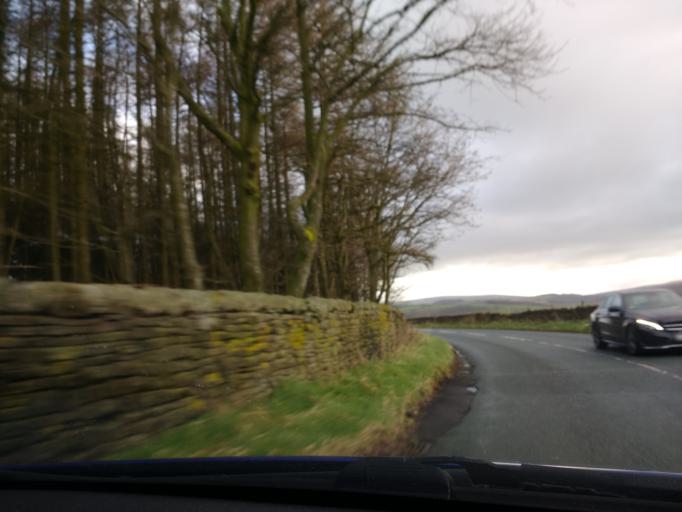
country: GB
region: England
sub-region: Lancashire
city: Lancaster
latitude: 54.0439
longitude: -2.7557
